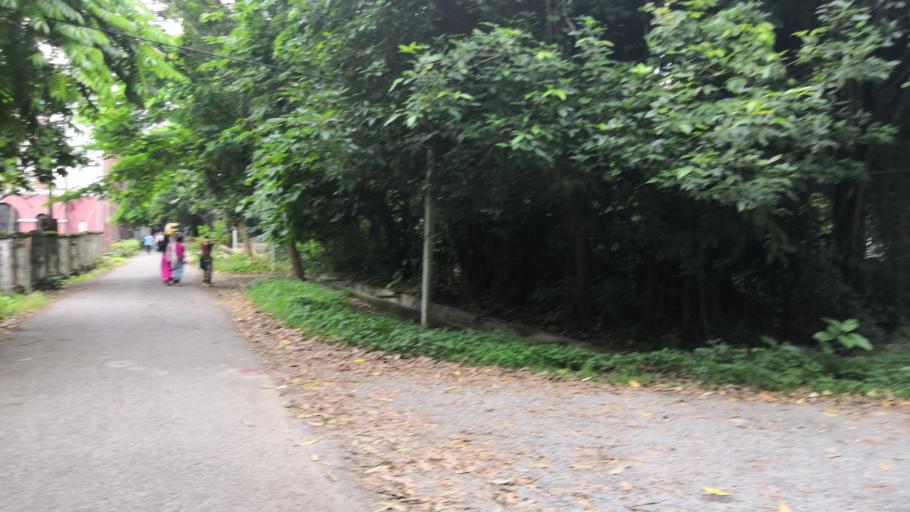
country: MM
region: Yangon
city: Yangon
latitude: 16.8296
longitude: 96.1334
